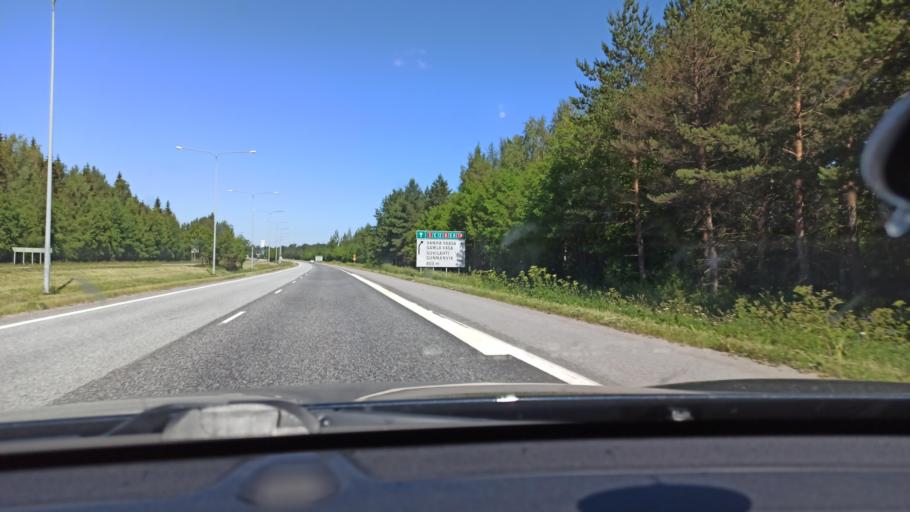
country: FI
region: Ostrobothnia
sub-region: Vaasa
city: Ristinummi
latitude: 63.0598
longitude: 21.7103
